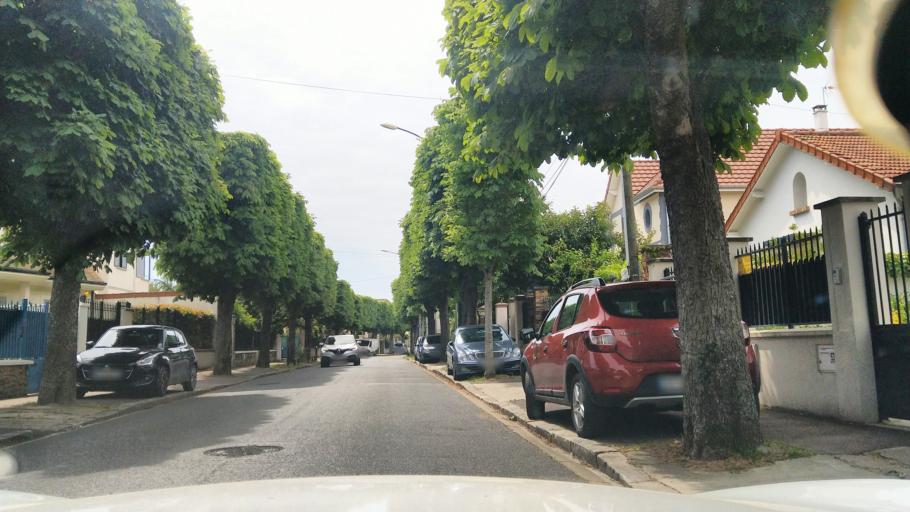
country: FR
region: Ile-de-France
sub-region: Departement du Val-de-Marne
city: Saint-Maur-des-Fosses
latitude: 48.7999
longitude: 2.5090
